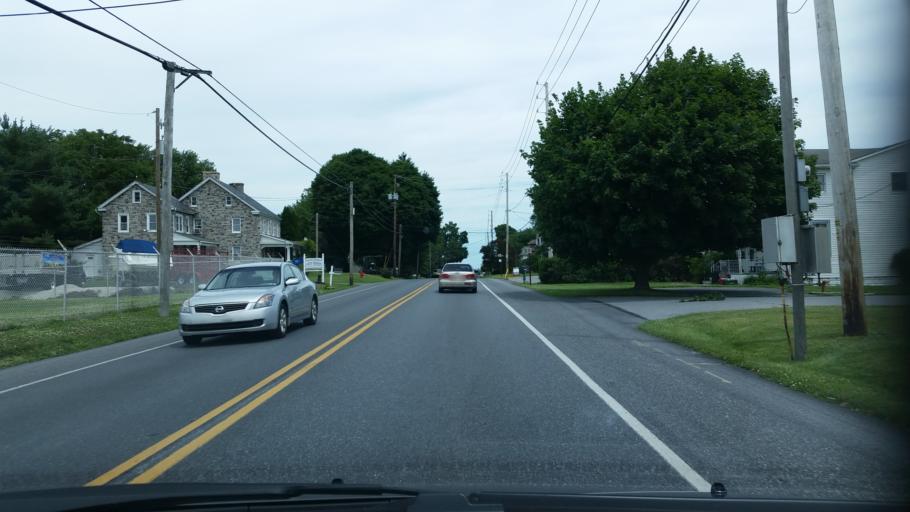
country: US
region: Pennsylvania
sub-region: Lancaster County
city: Lampeter
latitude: 40.0398
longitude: -76.2186
